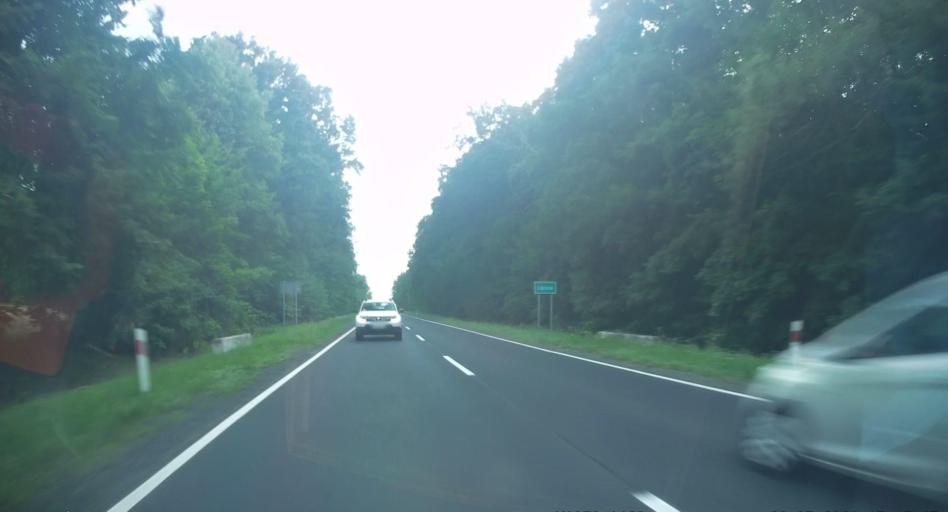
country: PL
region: Silesian Voivodeship
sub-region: Powiat czestochowski
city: Klomnice
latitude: 50.9523
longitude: 19.3998
